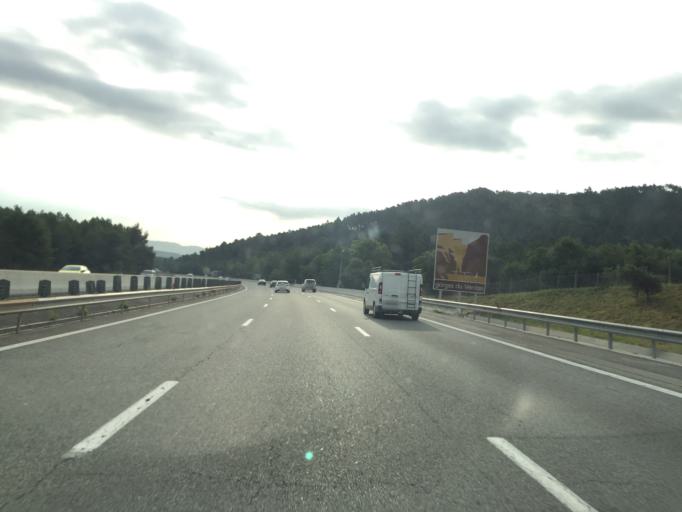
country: FR
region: Provence-Alpes-Cote d'Azur
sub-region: Departement du Var
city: Les Arcs
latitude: 43.4520
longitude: 6.5204
